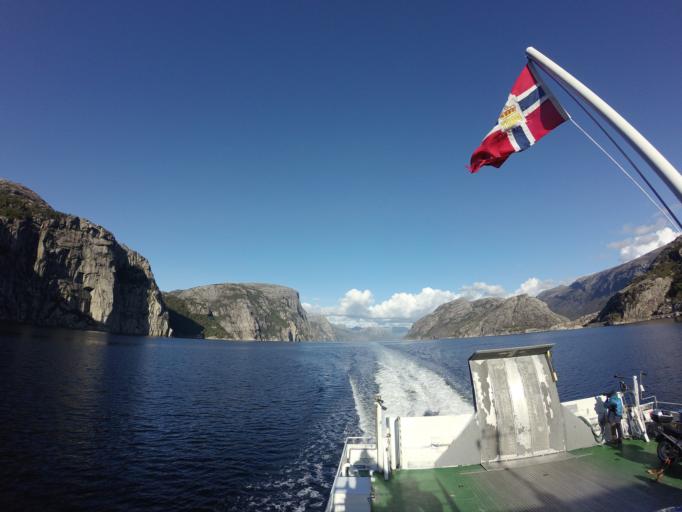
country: NO
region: Rogaland
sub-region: Forsand
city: Forsand
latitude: 58.9563
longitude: 6.1462
